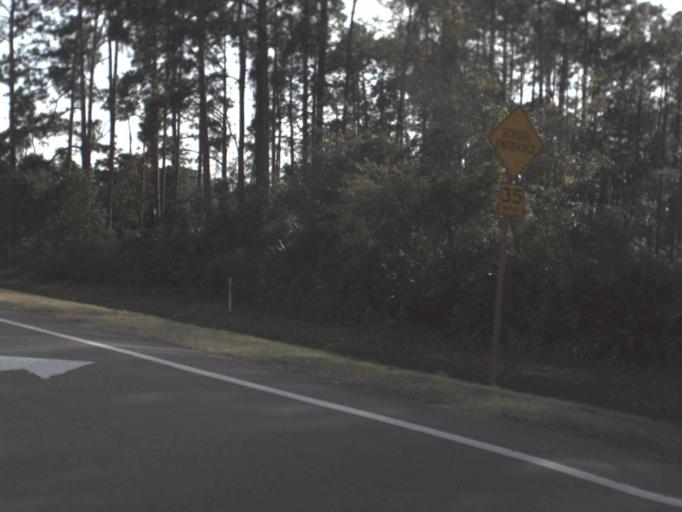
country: US
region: Florida
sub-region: Bay County
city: Tyndall Air Force Base
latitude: 30.0860
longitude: -85.6093
